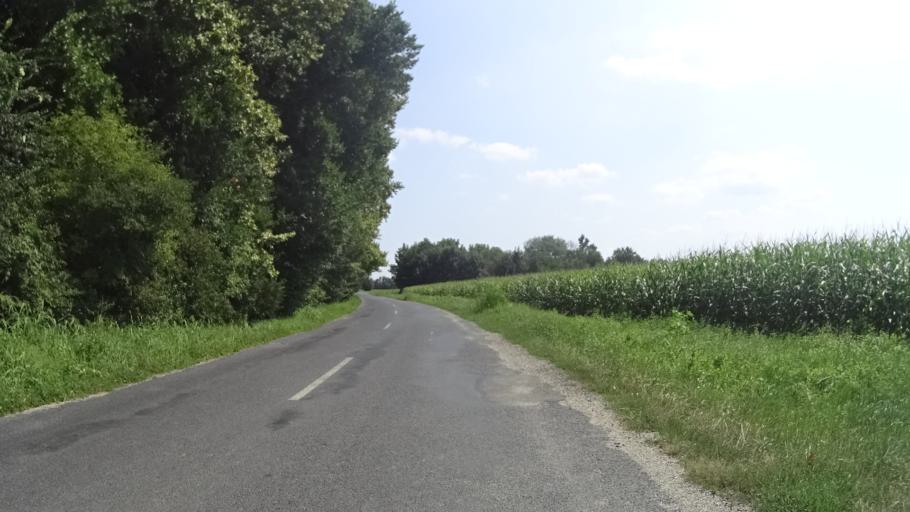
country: HU
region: Zala
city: Murakeresztur
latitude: 46.3683
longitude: 16.8628
